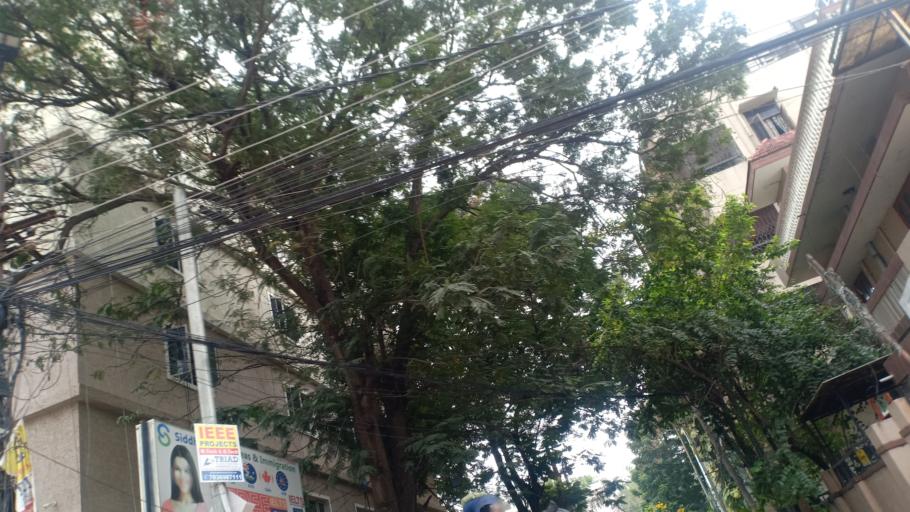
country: IN
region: Telangana
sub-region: Hyderabad
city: Hyderabad
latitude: 17.4321
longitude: 78.4449
